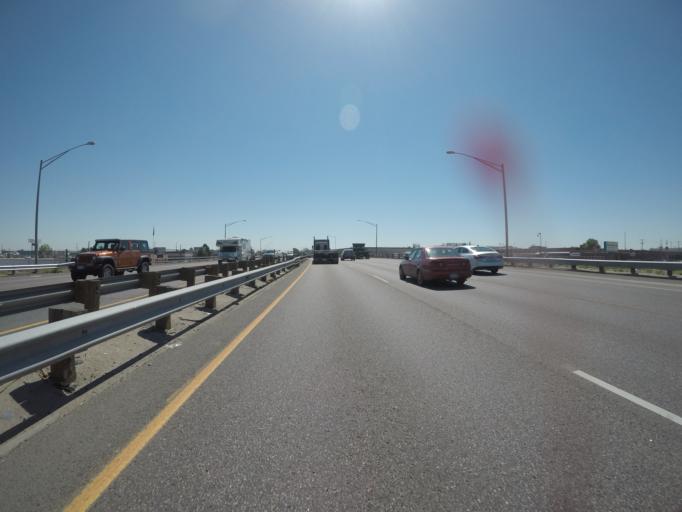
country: US
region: Colorado
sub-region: Adams County
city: Commerce City
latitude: 39.7784
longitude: -104.9229
